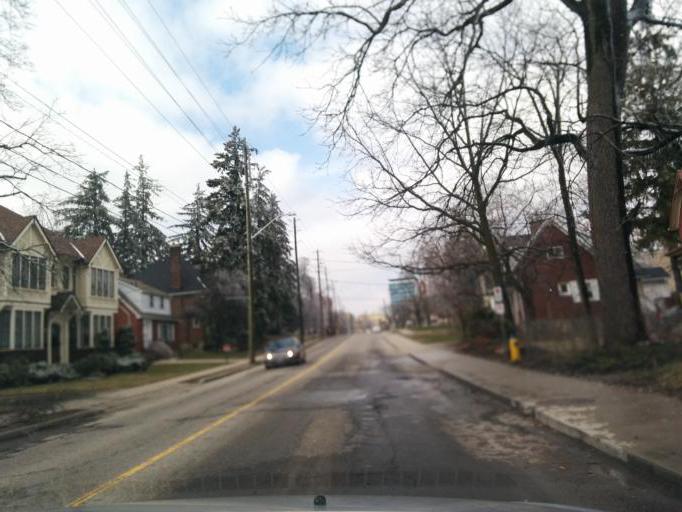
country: CA
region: Ontario
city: Waterloo
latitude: 43.4709
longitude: -80.5284
